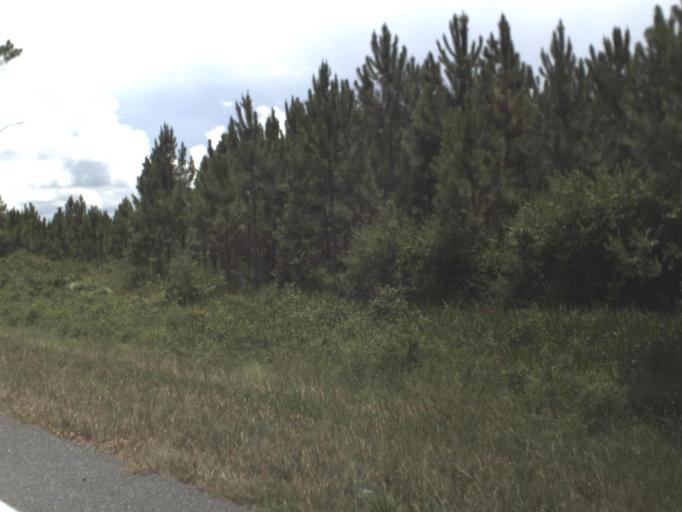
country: US
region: Florida
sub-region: Taylor County
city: Perry
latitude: 30.1428
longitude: -83.8258
